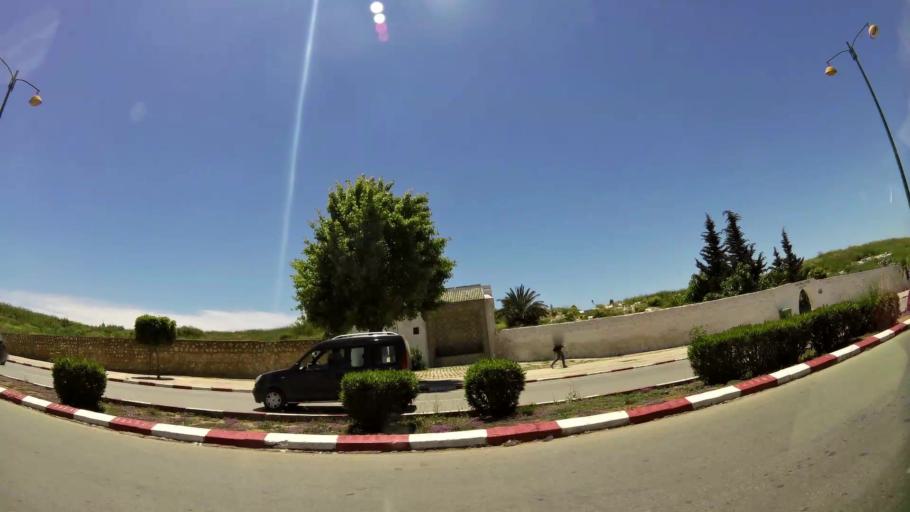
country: MA
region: Meknes-Tafilalet
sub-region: Meknes
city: Meknes
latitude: 33.9029
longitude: -5.5701
